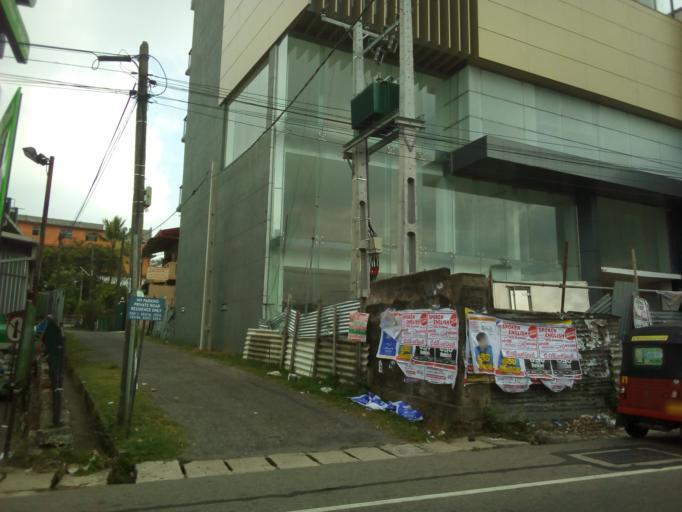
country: LK
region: Western
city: Sri Jayewardenepura Kotte
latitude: 6.8653
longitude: 79.8951
